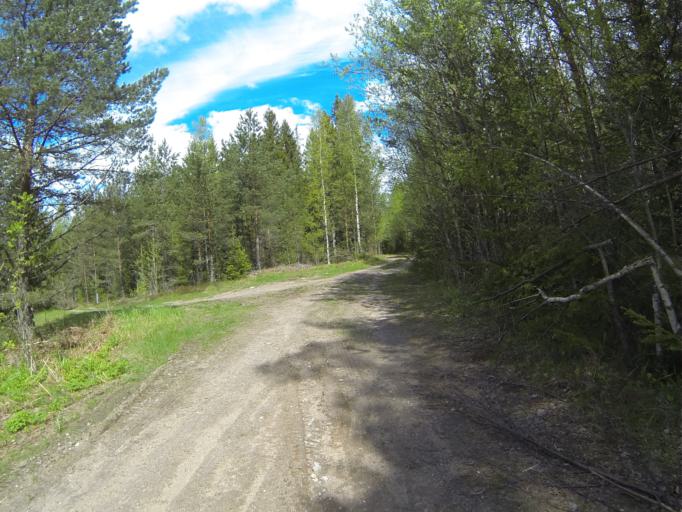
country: FI
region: Varsinais-Suomi
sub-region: Salo
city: Halikko
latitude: 60.3074
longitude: 23.0758
